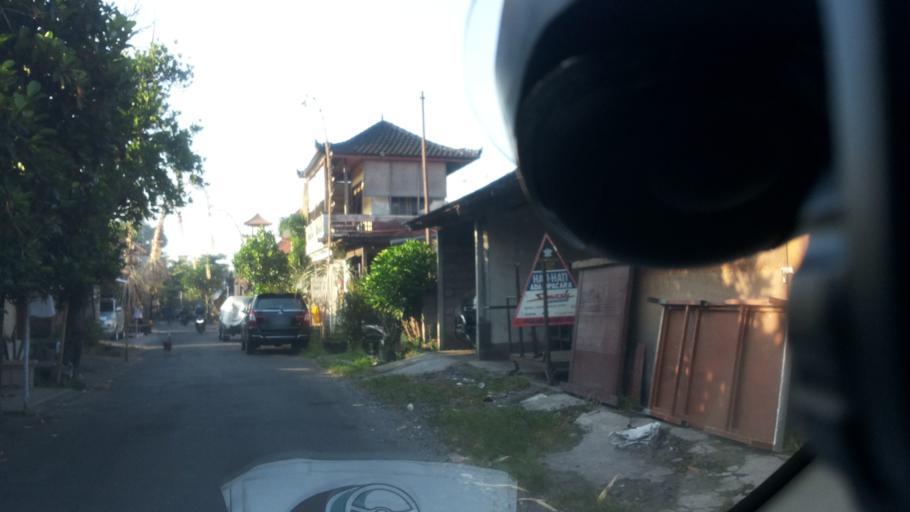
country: ID
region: Bali
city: Dajan Tangluk
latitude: -8.6440
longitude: 115.2412
